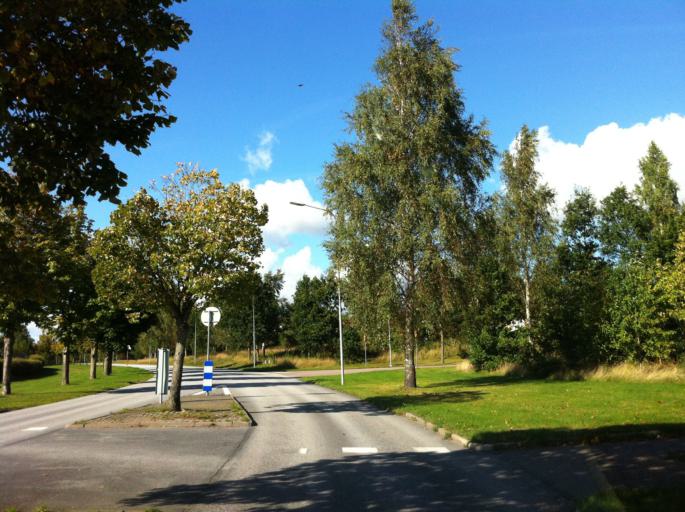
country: SE
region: Skane
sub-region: Sjobo Kommun
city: Sjoebo
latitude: 55.6378
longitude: 13.7303
